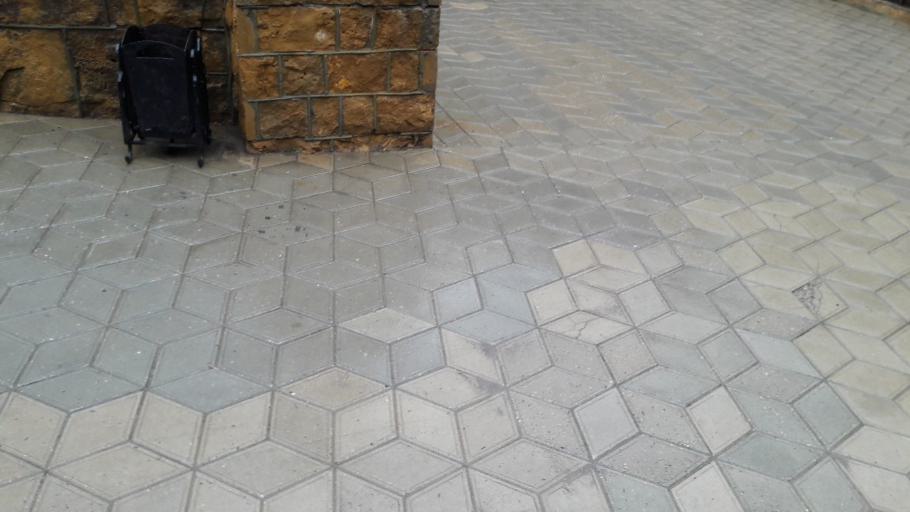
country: RU
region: Stavropol'skiy
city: Nezhinskiy
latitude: 43.8974
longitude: 42.6657
